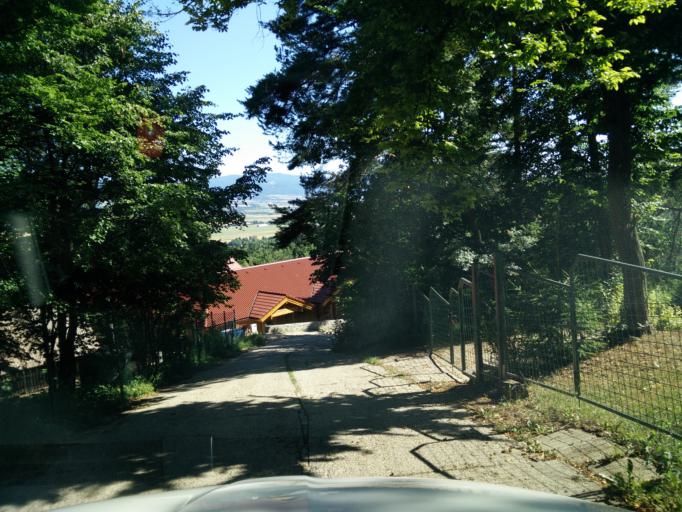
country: SK
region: Nitriansky
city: Bojnice
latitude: 48.7895
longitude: 18.5759
